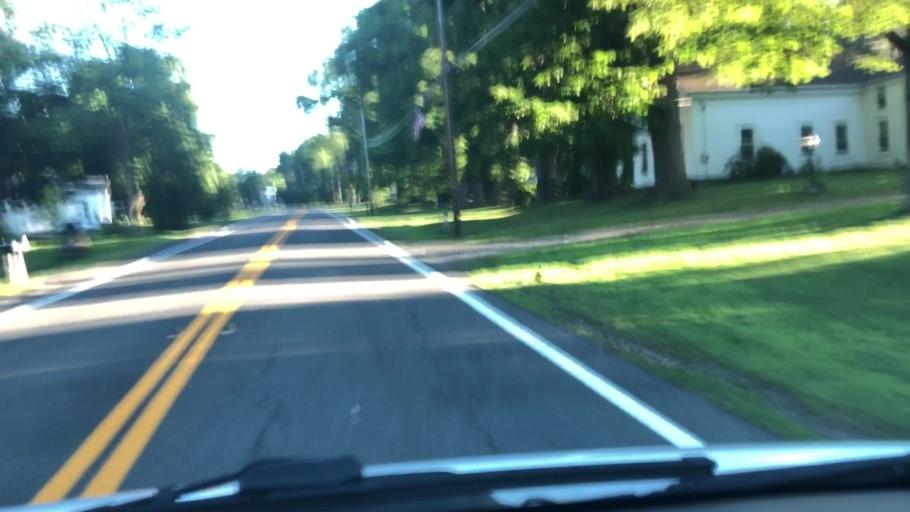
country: US
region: Massachusetts
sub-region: Hampshire County
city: Chesterfield
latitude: 42.3959
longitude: -72.9356
